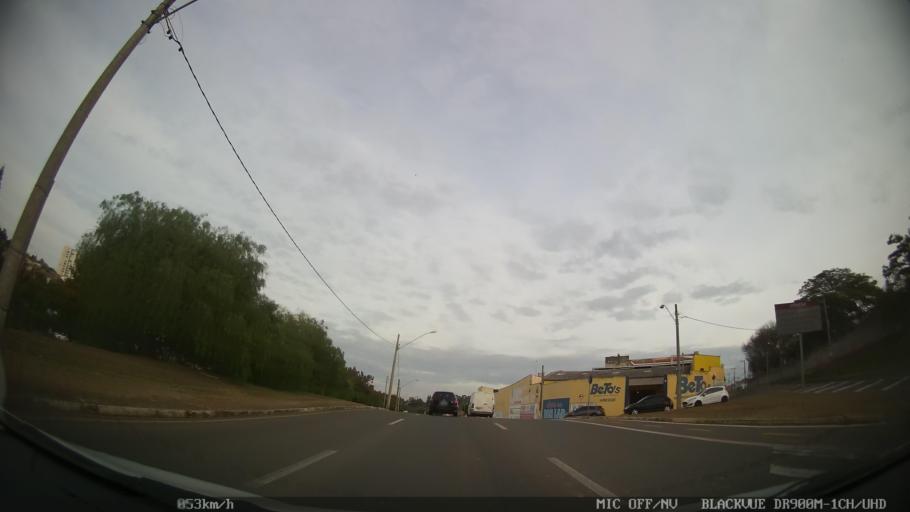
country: BR
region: Sao Paulo
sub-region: Limeira
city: Limeira
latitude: -22.5792
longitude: -47.4131
